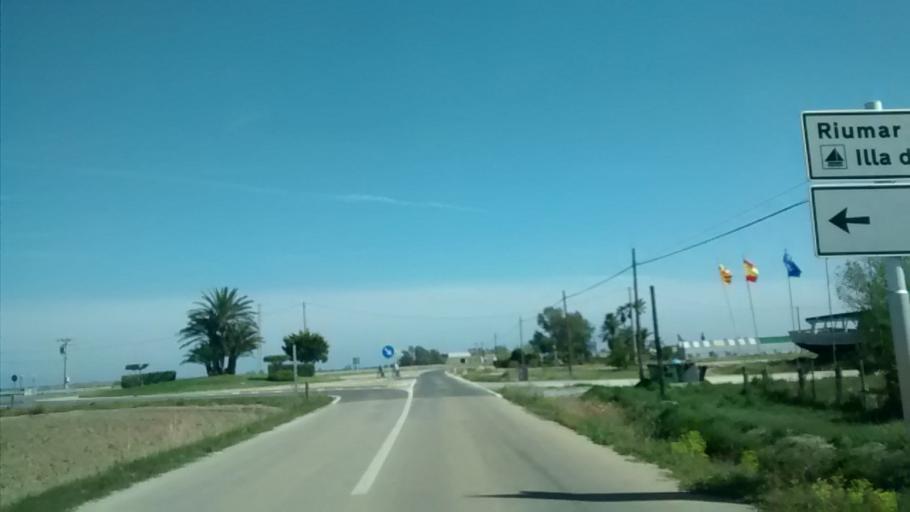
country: ES
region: Catalonia
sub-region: Provincia de Tarragona
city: Deltebre
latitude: 40.7120
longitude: 0.7551
